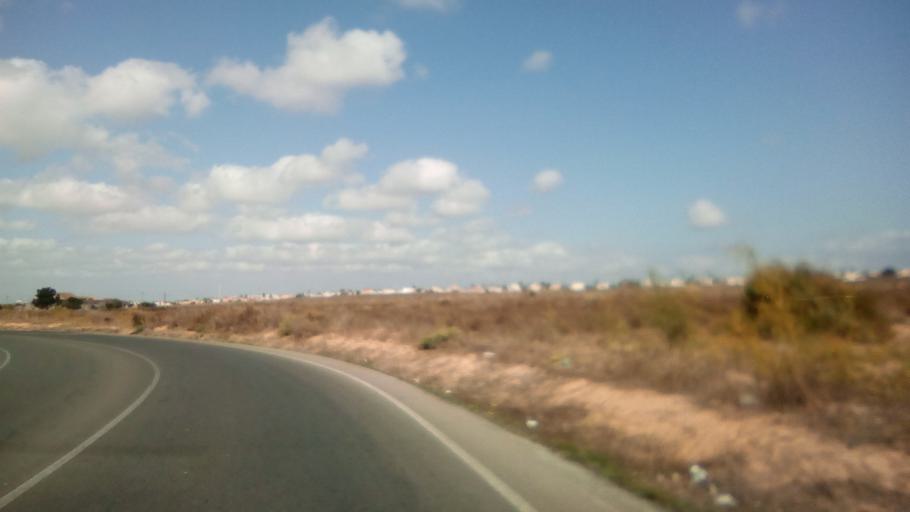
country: ES
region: Valencia
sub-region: Provincia de Alicante
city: Torrevieja
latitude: 38.0000
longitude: -0.6861
